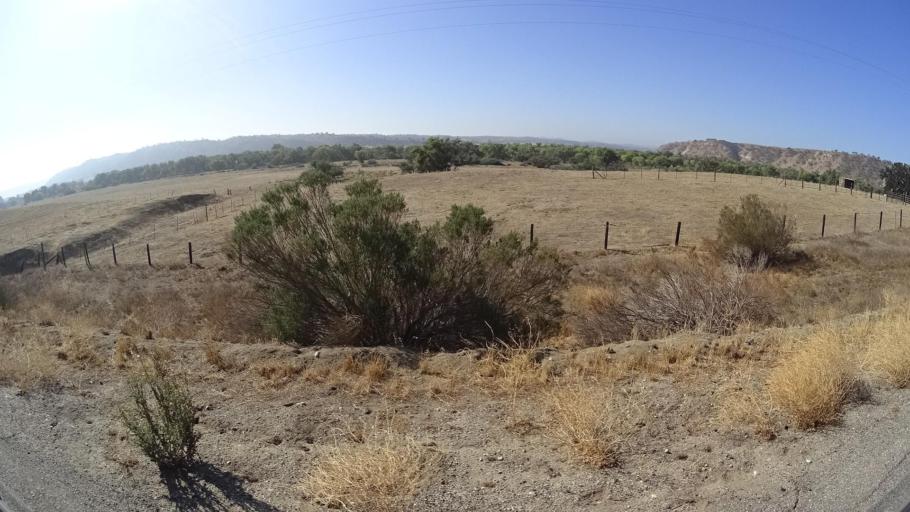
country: US
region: California
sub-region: San Luis Obispo County
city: San Miguel
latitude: 35.8624
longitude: -120.7950
